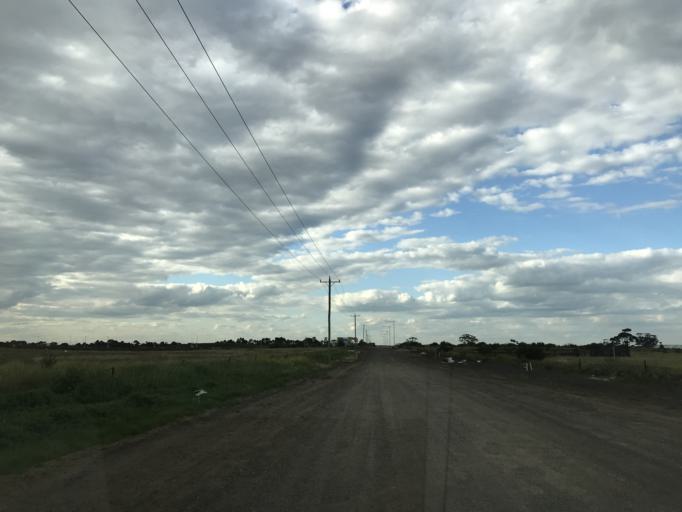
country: AU
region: Victoria
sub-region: Wyndham
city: Truganina
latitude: -37.8173
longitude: 144.7221
